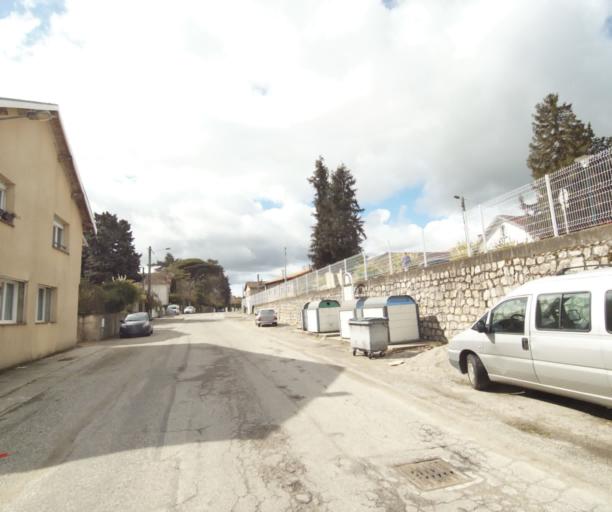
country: FR
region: Midi-Pyrenees
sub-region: Departement de l'Ariege
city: Saverdun
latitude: 43.2320
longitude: 1.5740
